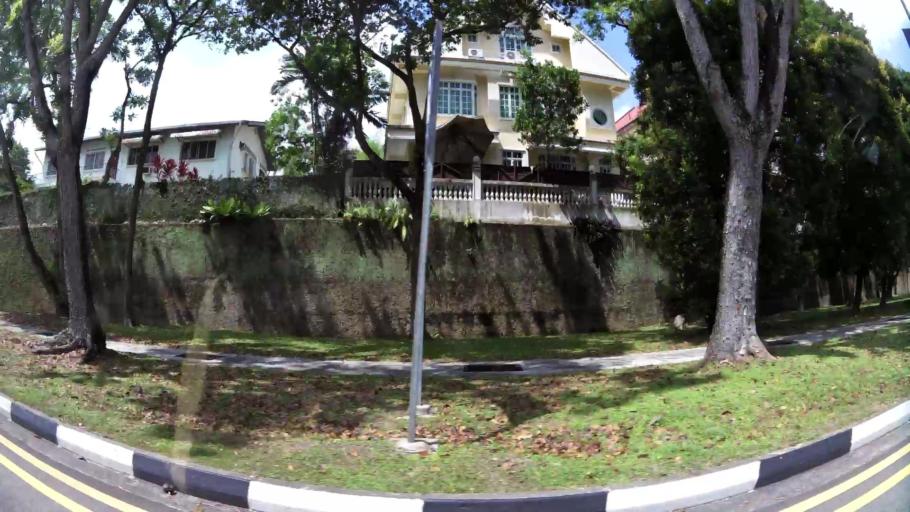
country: SG
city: Singapore
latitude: 1.3442
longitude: 103.8382
